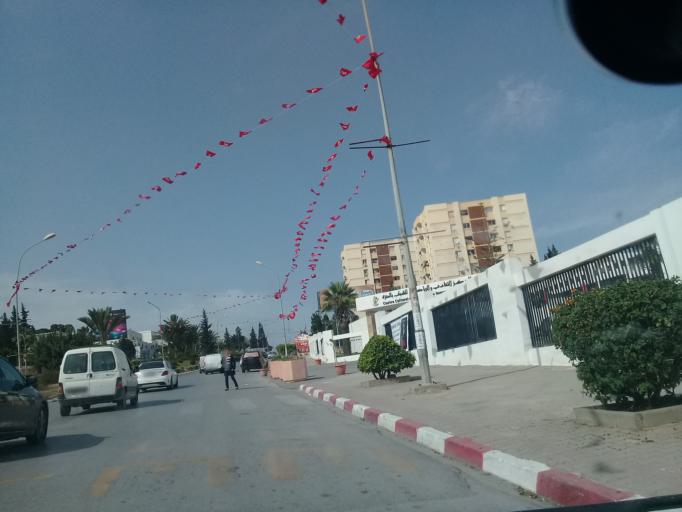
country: TN
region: Tunis
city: Tunis
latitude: 36.8468
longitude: 10.1677
